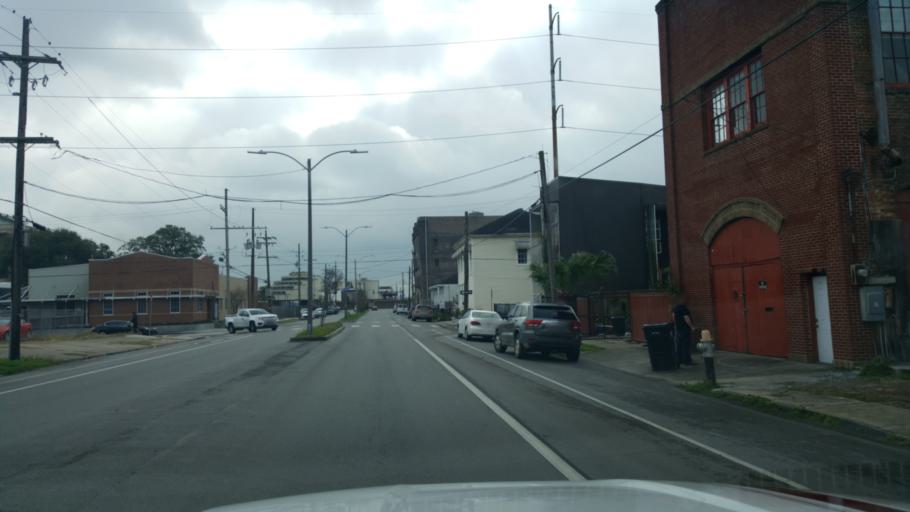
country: US
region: Louisiana
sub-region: Jefferson Parish
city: Gretna
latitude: 29.9251
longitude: -90.0729
